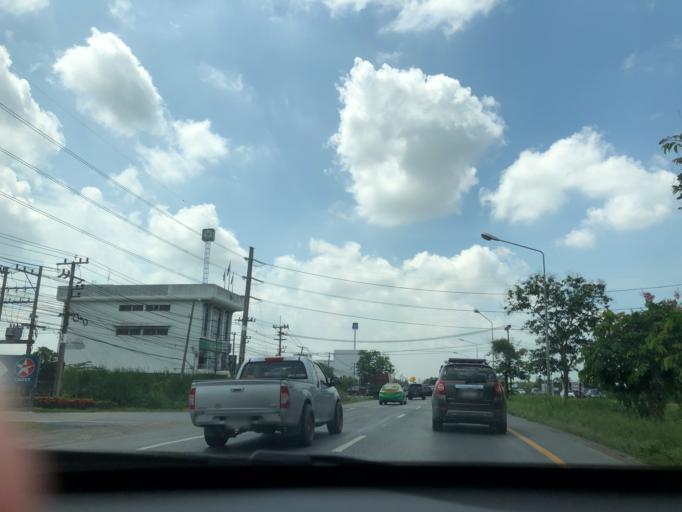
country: TH
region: Pathum Thani
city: Lat Lum Kaeo
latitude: 14.0257
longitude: 100.3553
